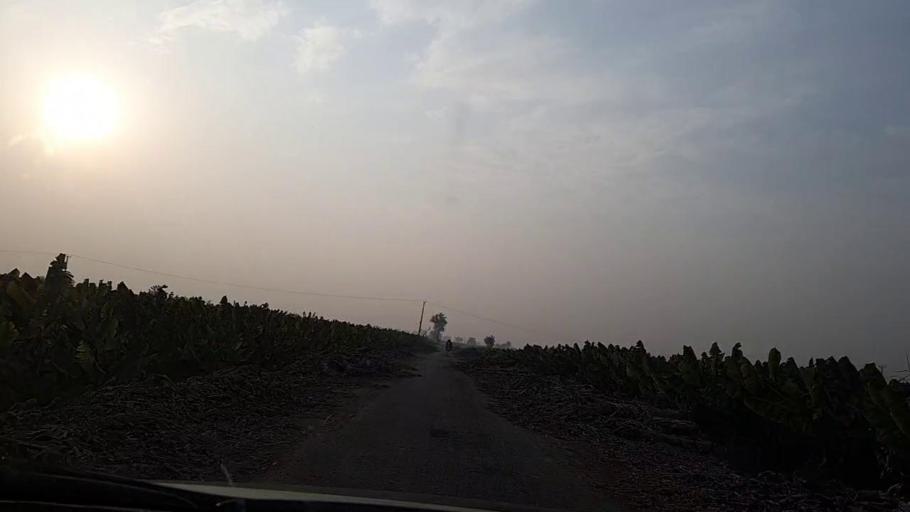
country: PK
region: Sindh
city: Nawabshah
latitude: 26.2967
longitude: 68.2739
